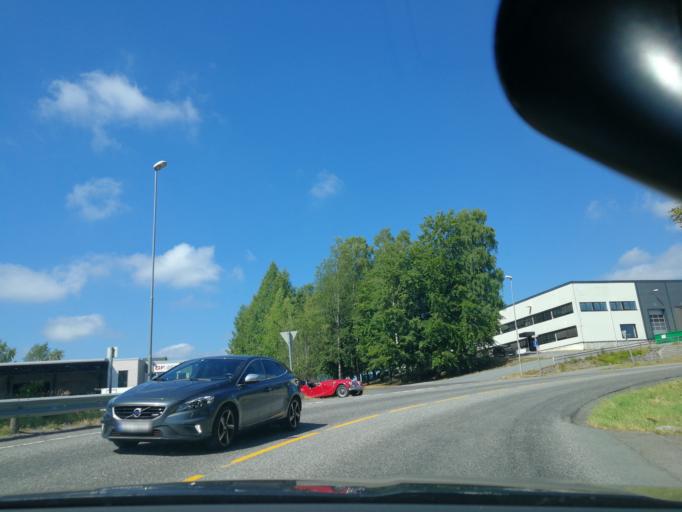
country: NO
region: Vestfold
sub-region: Sandefjord
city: Sandefjord
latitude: 59.1737
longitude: 10.2105
